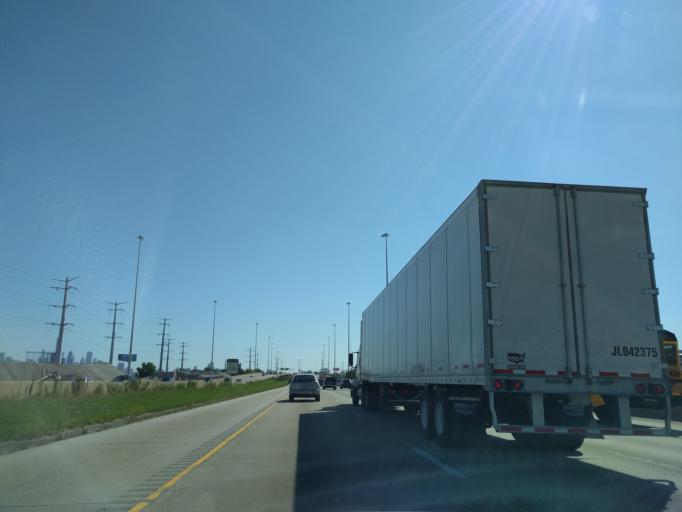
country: US
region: Illinois
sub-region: Cook County
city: Chicago
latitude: 41.8328
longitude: -87.6930
